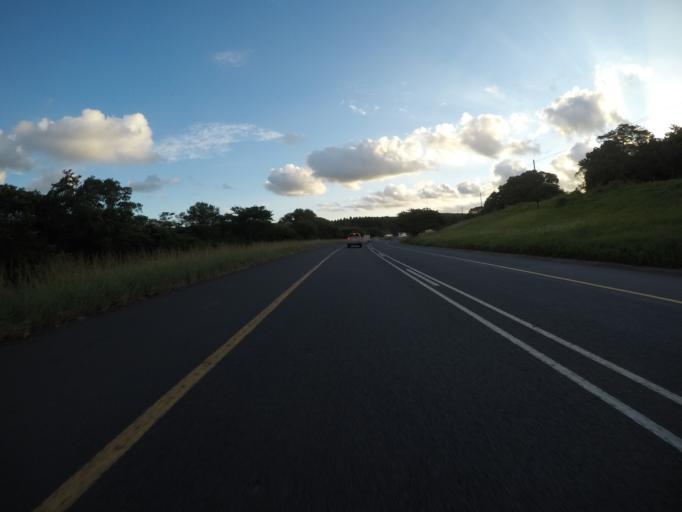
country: ZA
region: KwaZulu-Natal
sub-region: uThungulu District Municipality
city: Richards Bay
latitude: -28.6902
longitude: 32.0377
